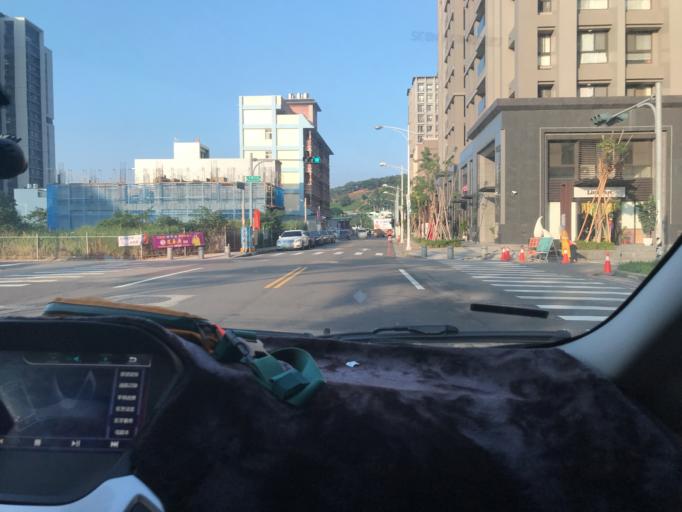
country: TW
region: Taiwan
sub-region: Hsinchu
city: Zhubei
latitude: 24.8237
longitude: 121.0336
